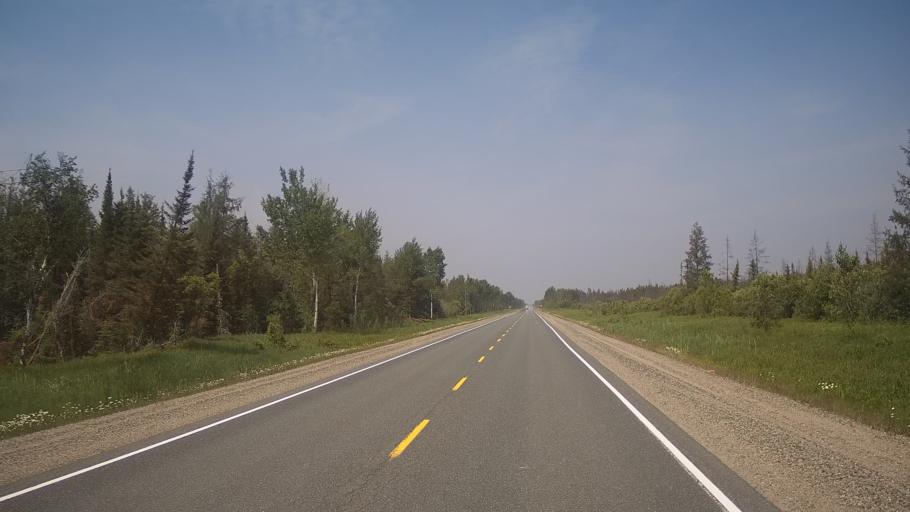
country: CA
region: Ontario
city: Timmins
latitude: 48.8048
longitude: -81.3681
